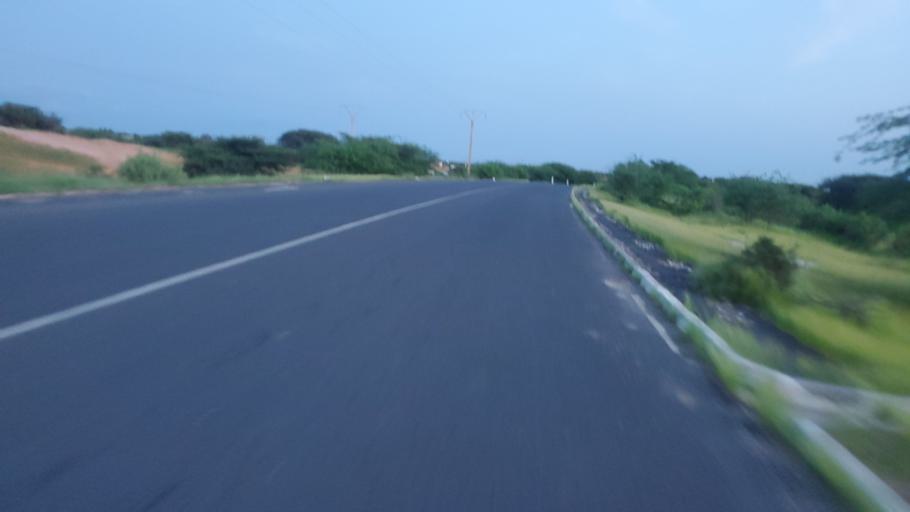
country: SN
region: Saint-Louis
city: Saint-Louis
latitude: 16.0757
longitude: -16.3895
